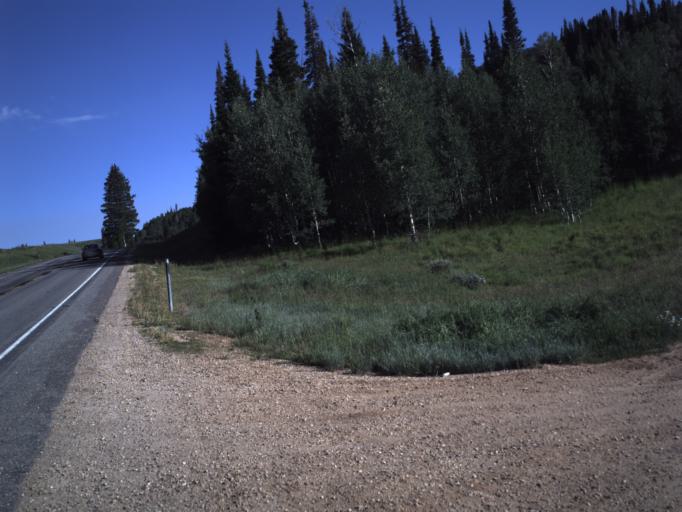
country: US
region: Utah
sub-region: Sanpete County
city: Fairview
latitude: 39.5990
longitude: -111.2715
